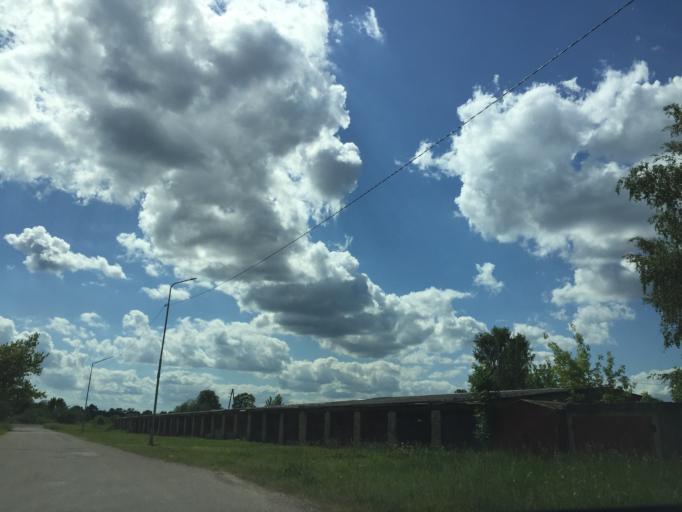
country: LV
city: Tireli
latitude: 56.8044
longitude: 23.5962
